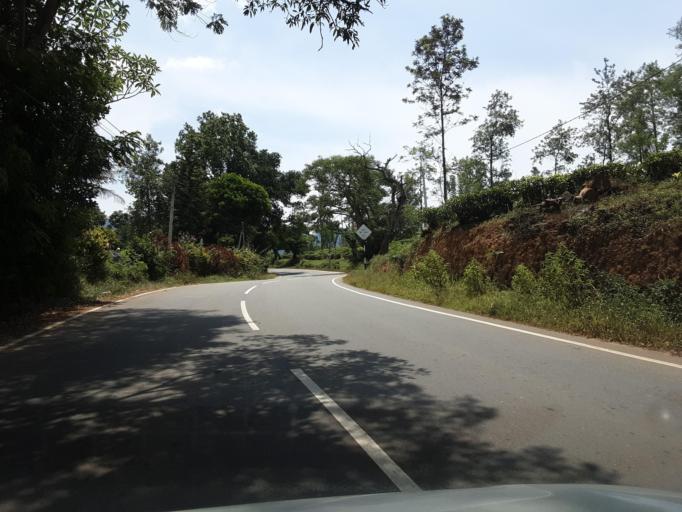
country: LK
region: Central
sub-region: Nuwara Eliya District
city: Nuwara Eliya
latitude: 6.9448
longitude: 80.9144
